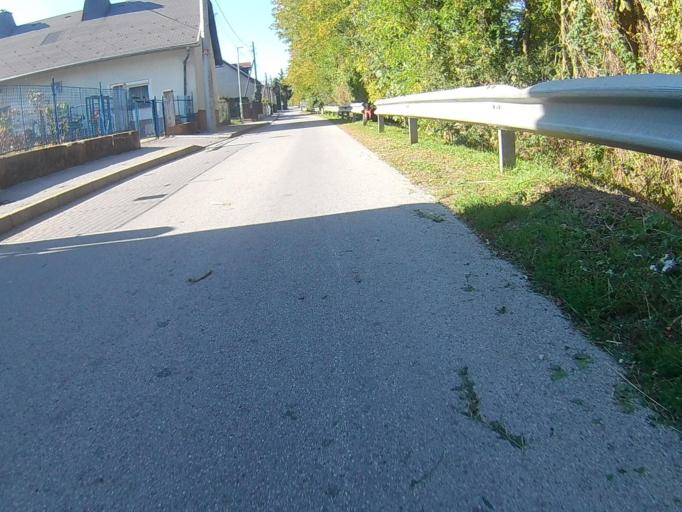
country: SI
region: Maribor
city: Kamnica
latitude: 46.5607
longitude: 15.6200
